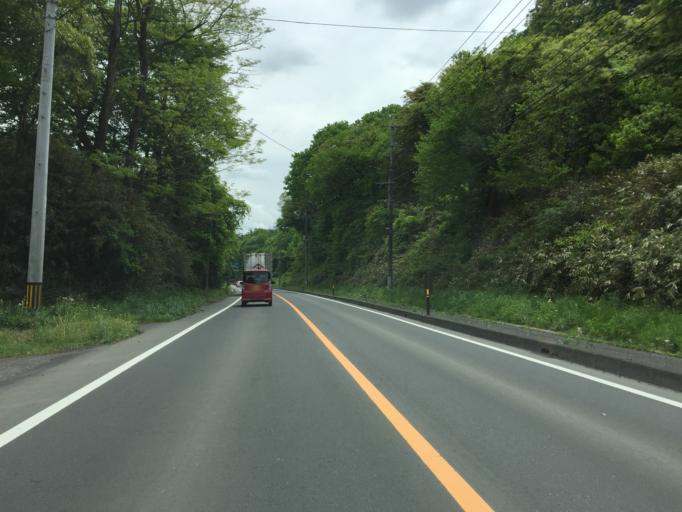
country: JP
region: Fukushima
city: Ishikawa
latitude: 37.0494
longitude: 140.3739
